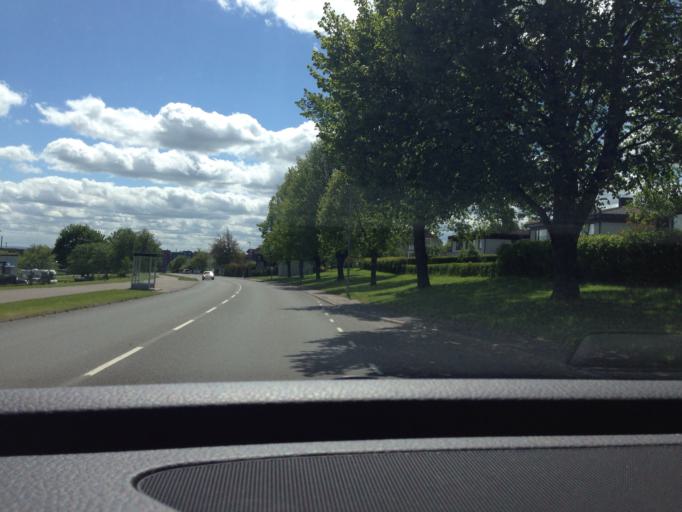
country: SE
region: Vaestra Goetaland
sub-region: Skovde Kommun
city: Skoevde
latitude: 58.4069
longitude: 13.8324
